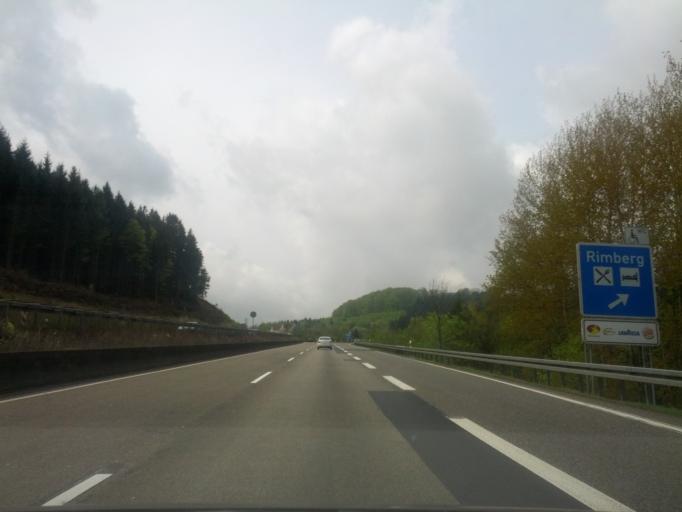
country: DE
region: Hesse
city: Grebenau
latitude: 50.7957
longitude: 9.4808
